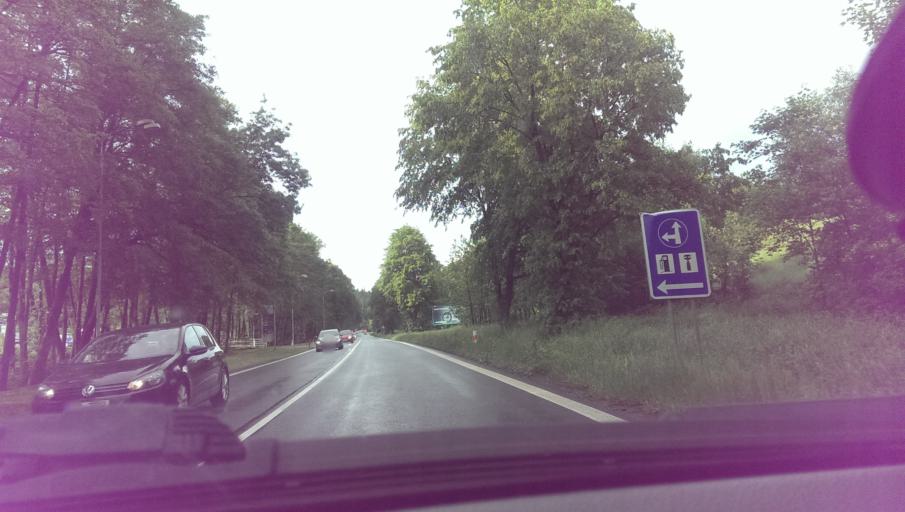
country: CZ
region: Zlin
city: Breznice
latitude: 49.1715
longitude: 17.6405
